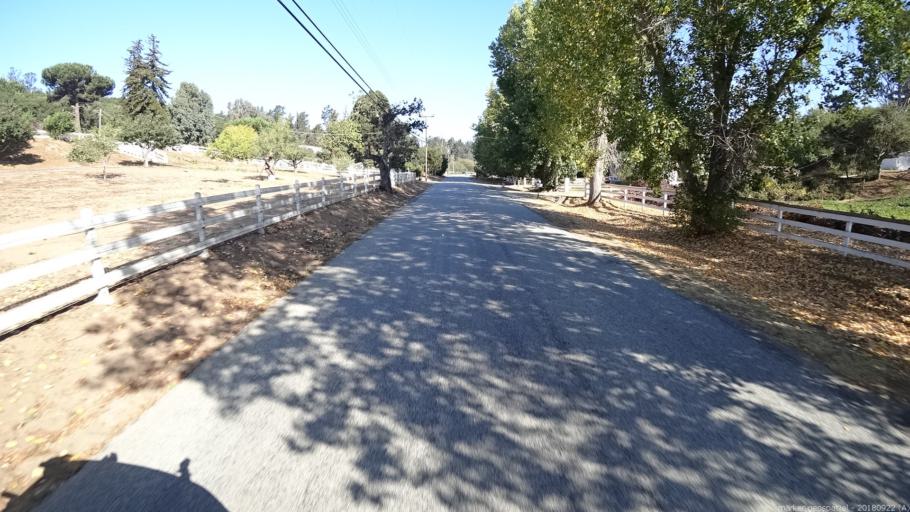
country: US
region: California
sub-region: Monterey County
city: Prunedale
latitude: 36.8104
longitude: -121.6500
